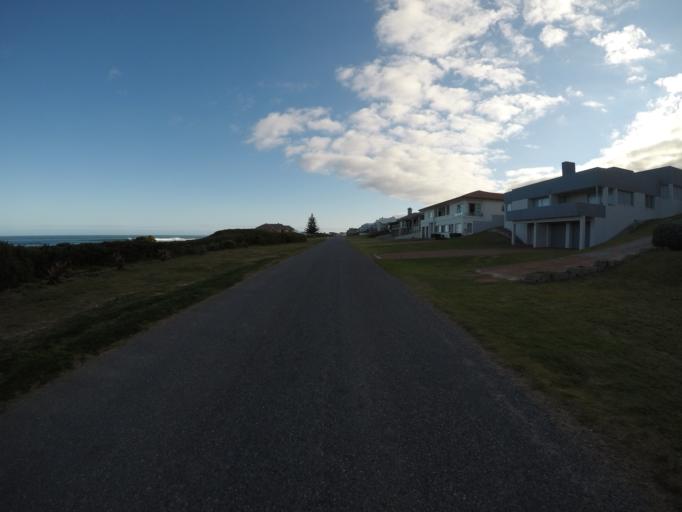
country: ZA
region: Western Cape
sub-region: Eden District Municipality
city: Riversdale
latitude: -34.4227
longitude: 21.3469
